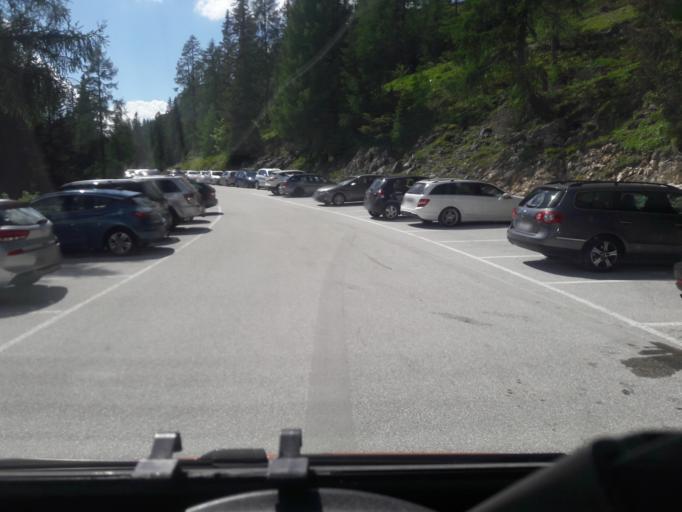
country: AT
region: Styria
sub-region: Politischer Bezirk Liezen
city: Tauplitz
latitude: 47.5936
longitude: 13.9852
